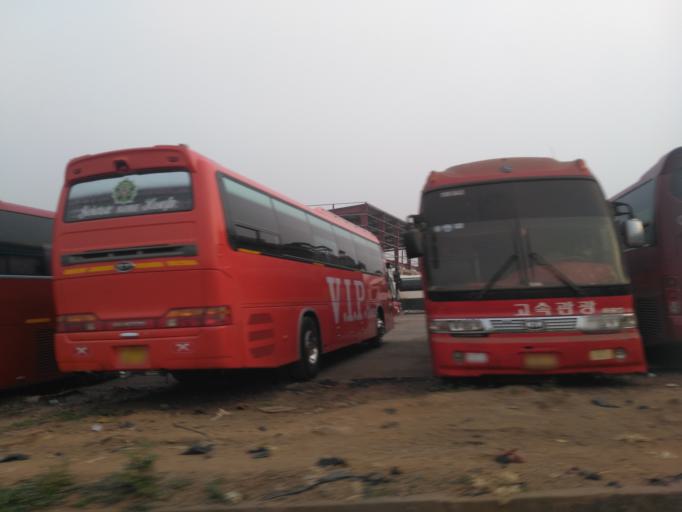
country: GH
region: Ashanti
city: Kumasi
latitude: 6.6804
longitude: -1.6131
